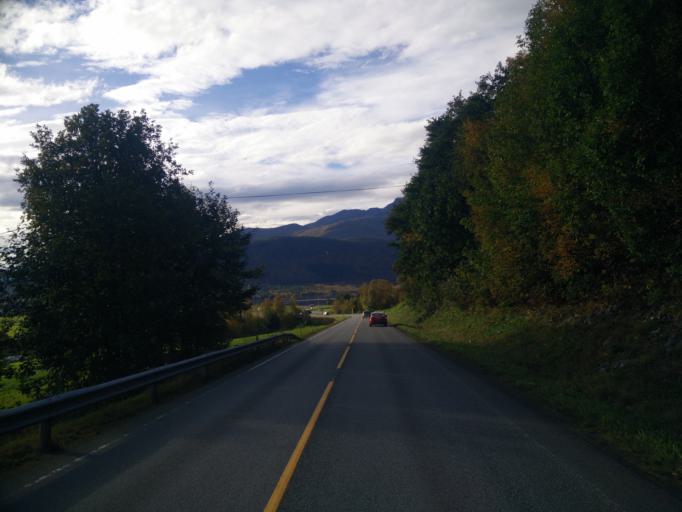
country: NO
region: More og Romsdal
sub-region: Vestnes
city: Vestnes
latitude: 62.6339
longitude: 7.0752
